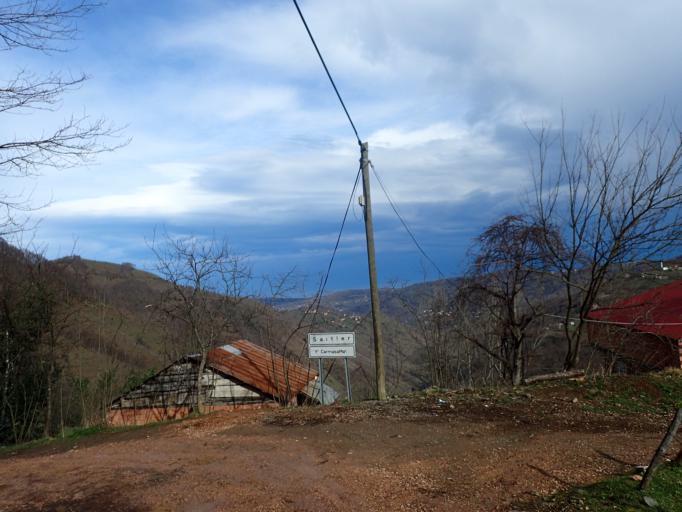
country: TR
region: Ordu
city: Camas
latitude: 40.8901
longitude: 37.5798
